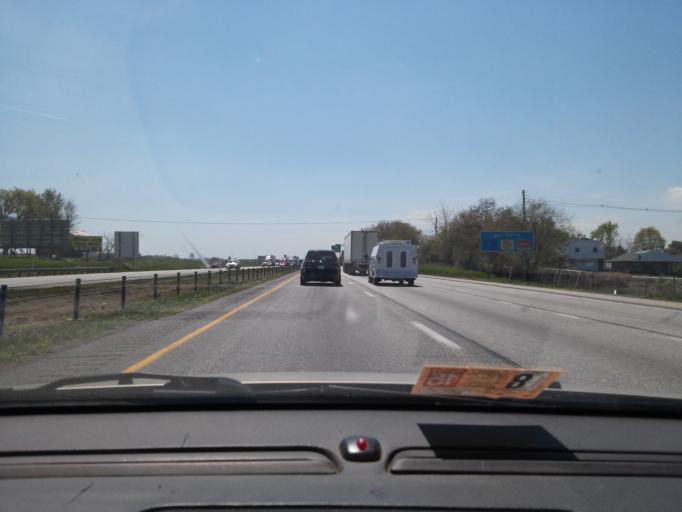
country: US
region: Pennsylvania
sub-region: Franklin County
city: Chambersburg
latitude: 39.9183
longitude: -77.6409
